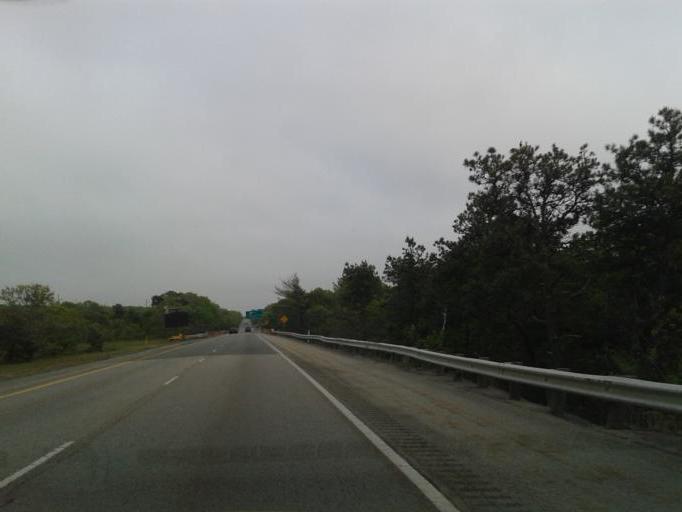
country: US
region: Massachusetts
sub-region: Barnstable County
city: Sagamore
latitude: 41.8150
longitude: -70.5547
